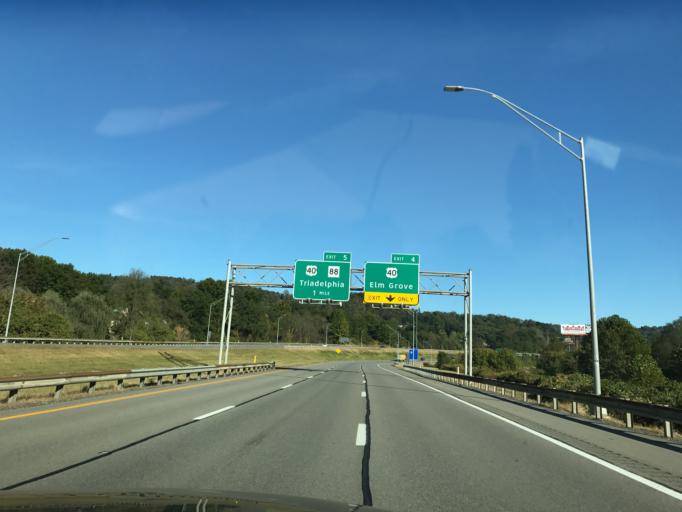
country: US
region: West Virginia
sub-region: Ohio County
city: Bethlehem
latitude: 40.0526
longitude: -80.6727
